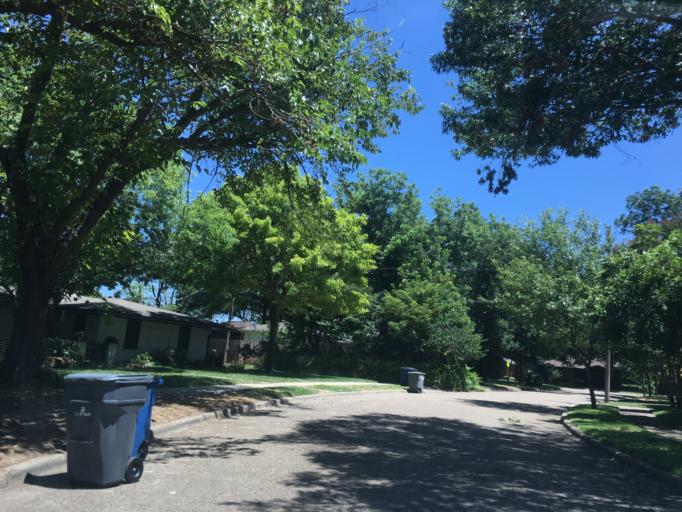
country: US
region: Texas
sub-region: Dallas County
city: Highland Park
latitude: 32.8484
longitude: -96.7078
